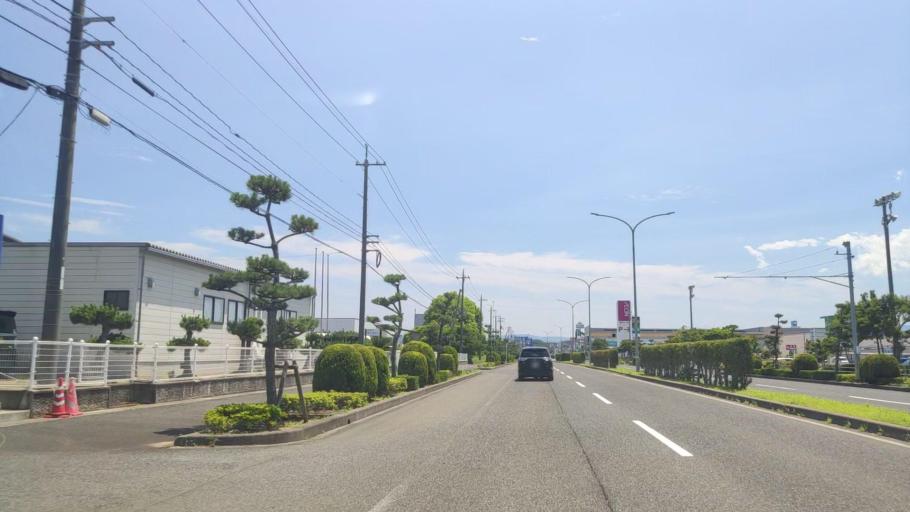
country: JP
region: Tottori
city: Tottori
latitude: 35.5245
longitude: 134.2028
